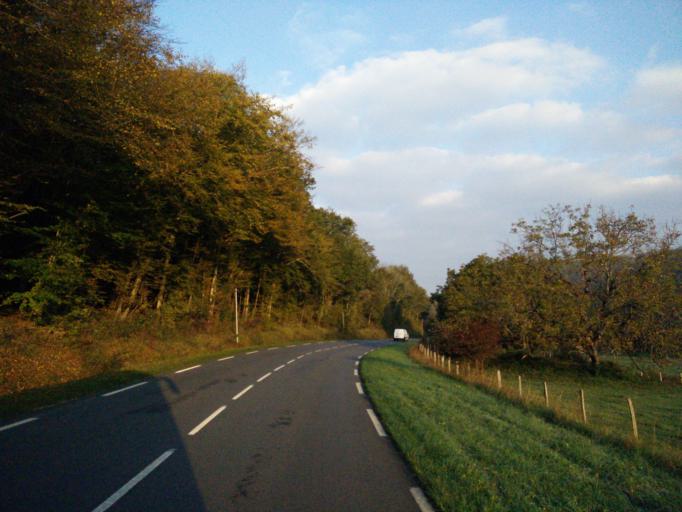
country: FR
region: Aquitaine
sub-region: Departement de la Dordogne
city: Le Bugue
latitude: 44.9627
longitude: 0.9734
